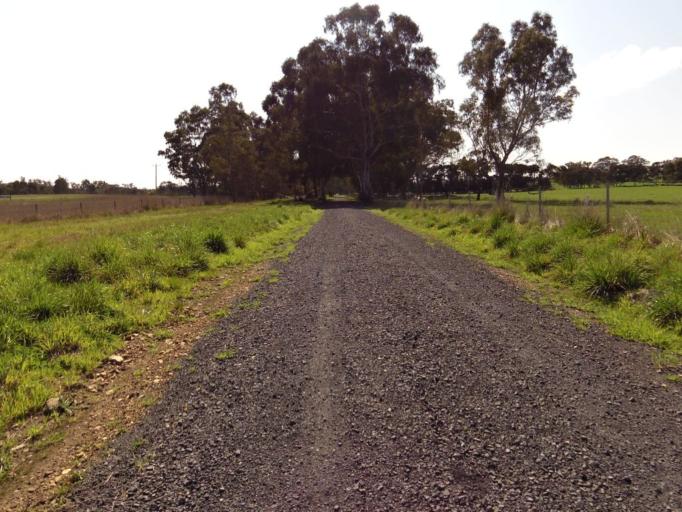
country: AU
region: Victoria
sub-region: Murrindindi
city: Alexandra
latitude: -37.1264
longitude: 145.5979
